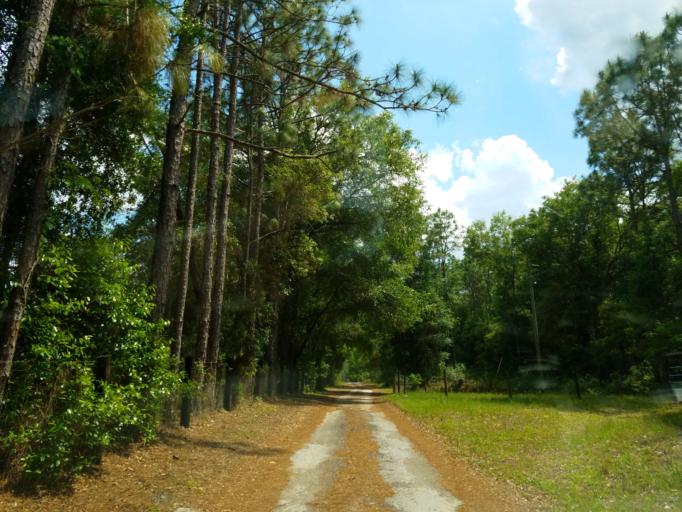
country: US
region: Florida
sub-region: Hernando County
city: Hill 'n Dale
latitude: 28.5314
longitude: -82.2550
